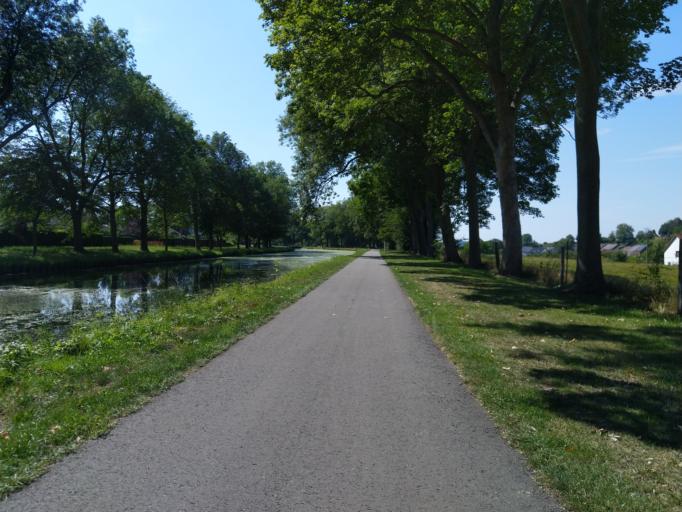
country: BE
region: Wallonia
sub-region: Province du Hainaut
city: Roeulx
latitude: 50.4752
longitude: 4.1170
